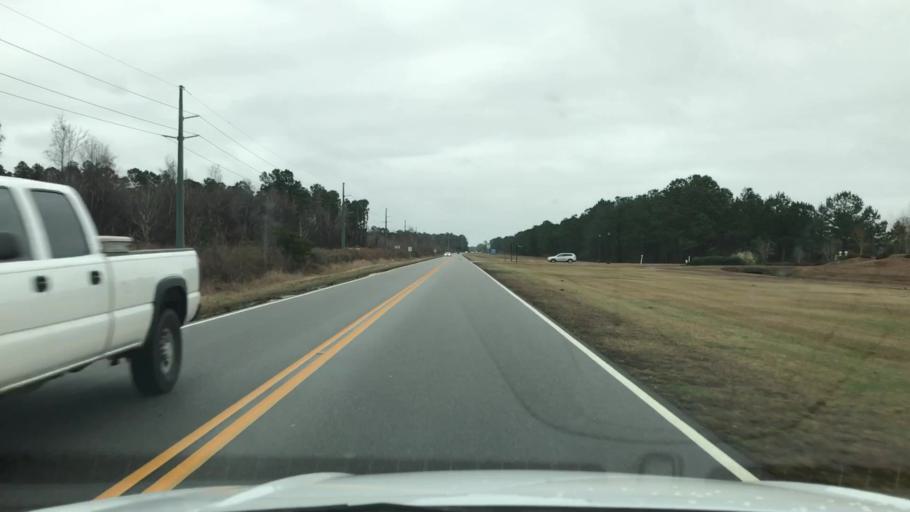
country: US
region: South Carolina
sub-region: Horry County
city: Myrtle Beach
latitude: 33.7384
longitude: -78.8935
